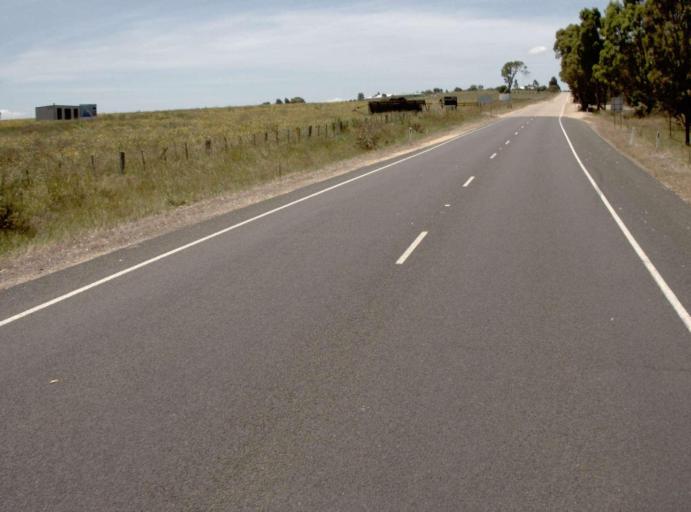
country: AU
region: Victoria
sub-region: East Gippsland
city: Bairnsdale
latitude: -37.8060
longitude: 147.6503
